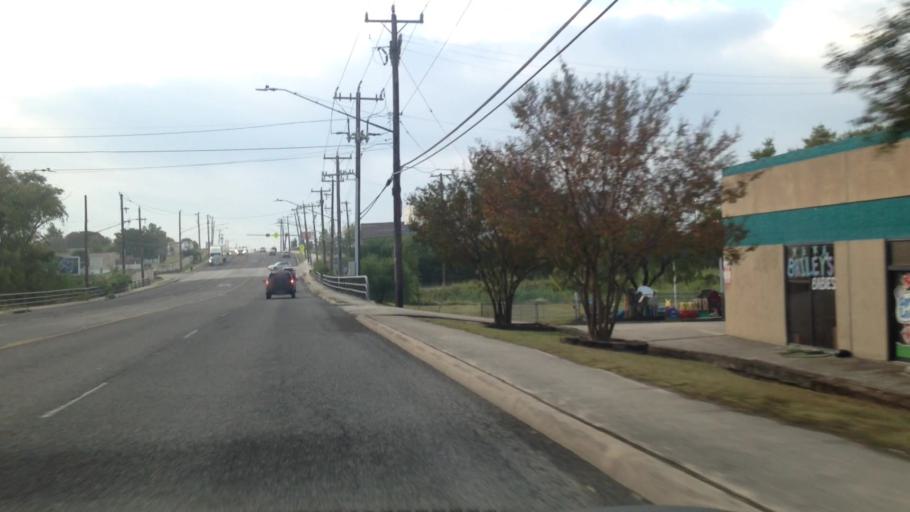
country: US
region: Texas
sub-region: Bexar County
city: Live Oak
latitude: 29.5651
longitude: -98.3641
